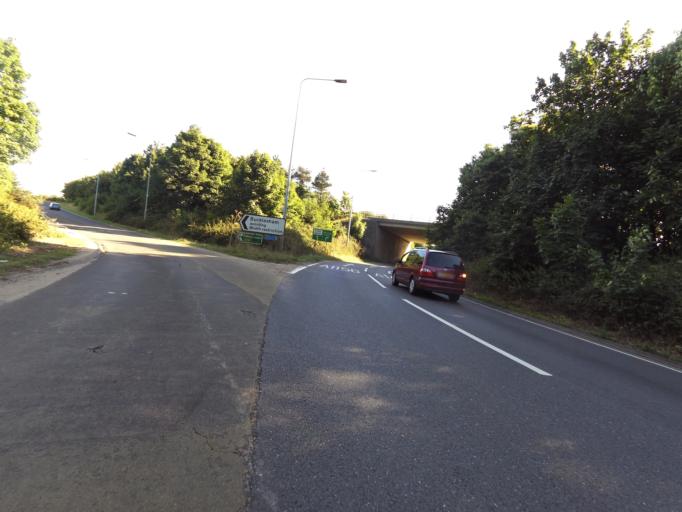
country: GB
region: England
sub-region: Suffolk
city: Kesgrave
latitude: 52.0261
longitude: 1.2558
